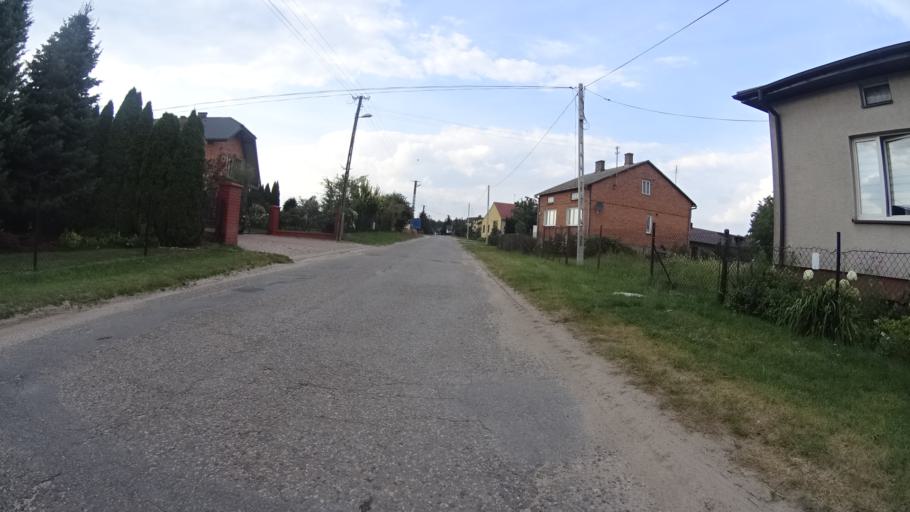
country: PL
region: Masovian Voivodeship
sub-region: Powiat grojecki
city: Mogielnica
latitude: 51.6696
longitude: 20.7408
